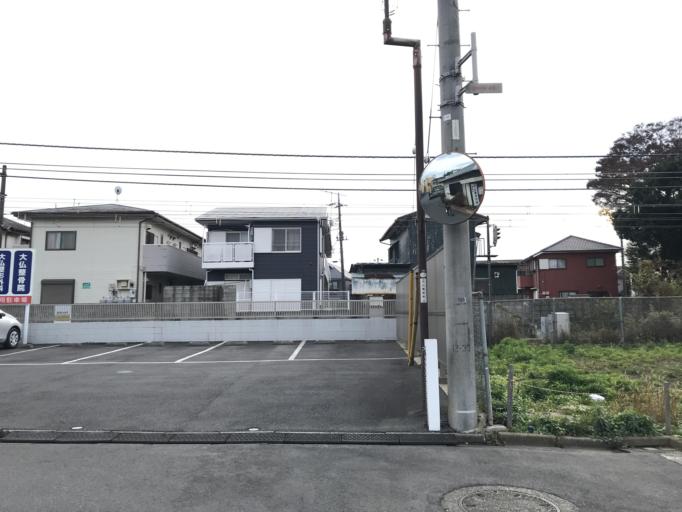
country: JP
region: Chiba
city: Shiroi
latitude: 35.7589
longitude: 140.0120
